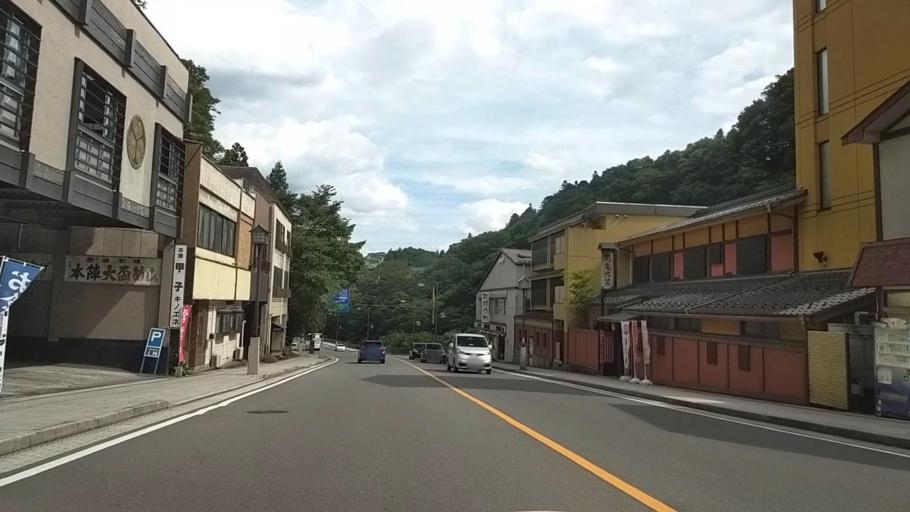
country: JP
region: Tochigi
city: Nikko
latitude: 36.7535
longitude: 139.5999
